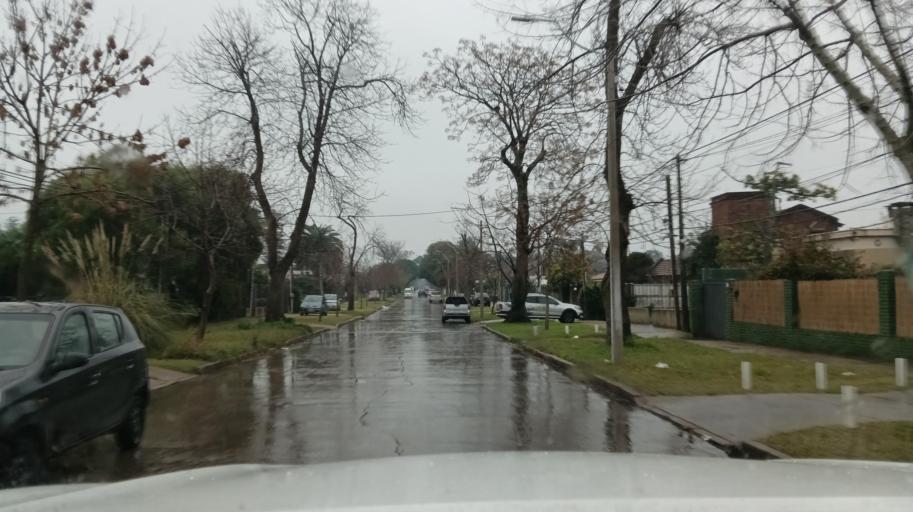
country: UY
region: Canelones
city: Paso de Carrasco
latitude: -34.8772
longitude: -56.0856
